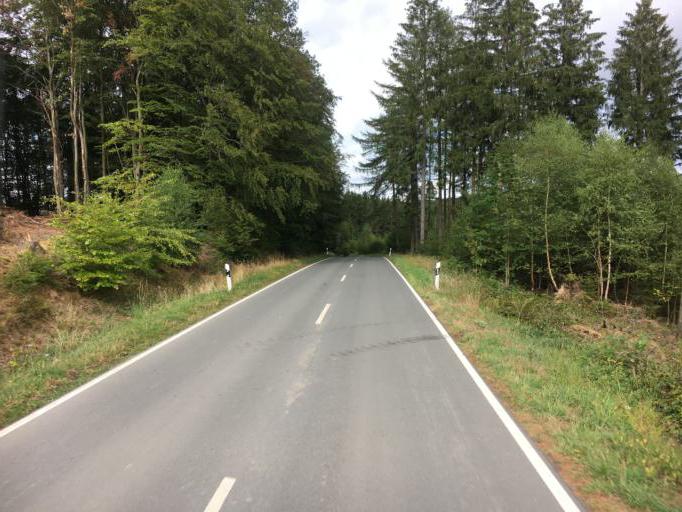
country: DE
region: North Rhine-Westphalia
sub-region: Regierungsbezirk Arnsberg
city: Herscheid
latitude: 51.2040
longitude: 7.7577
